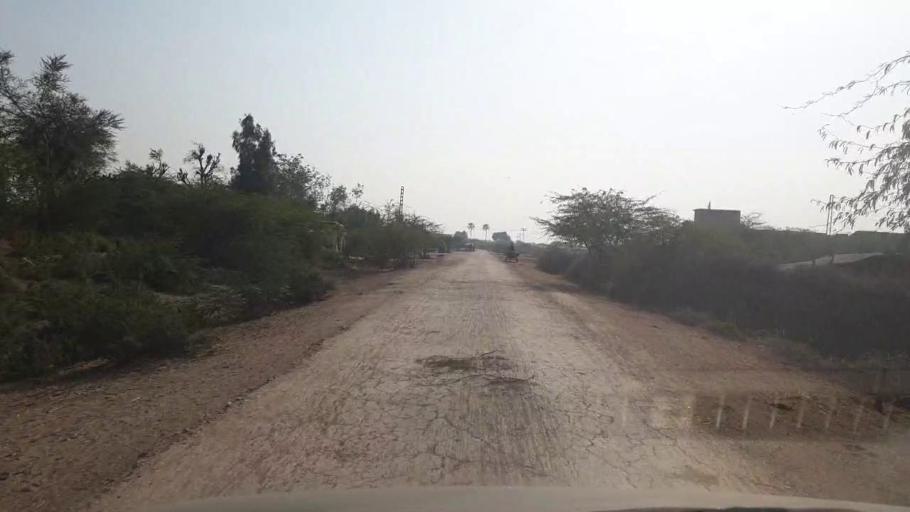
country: PK
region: Sindh
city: Digri
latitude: 25.2507
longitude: 69.1822
